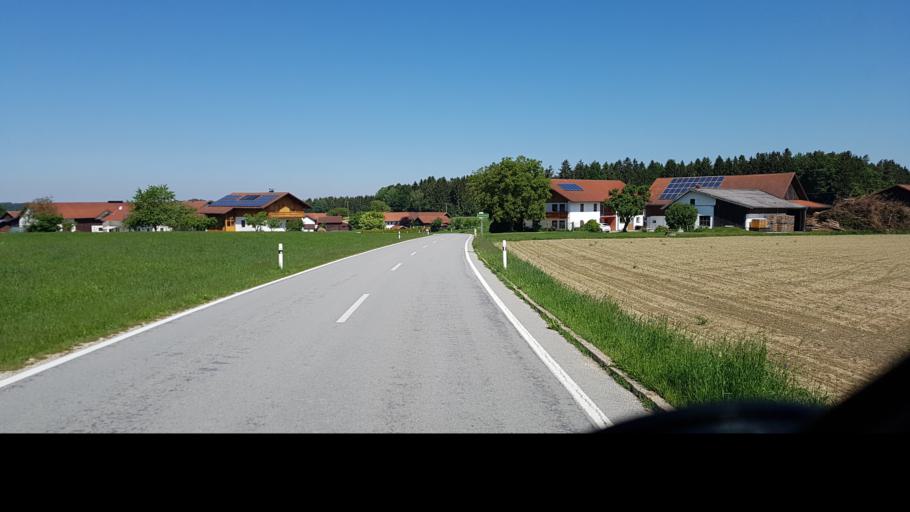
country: DE
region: Bavaria
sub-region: Lower Bavaria
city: Simbach am Inn
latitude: 48.3079
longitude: 13.0259
